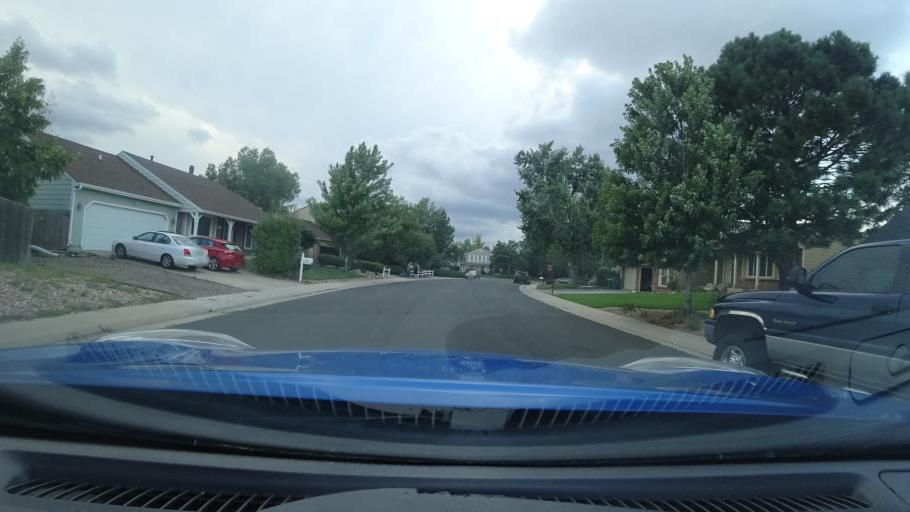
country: US
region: Colorado
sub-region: Adams County
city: Aurora
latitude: 39.6937
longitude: -104.8029
